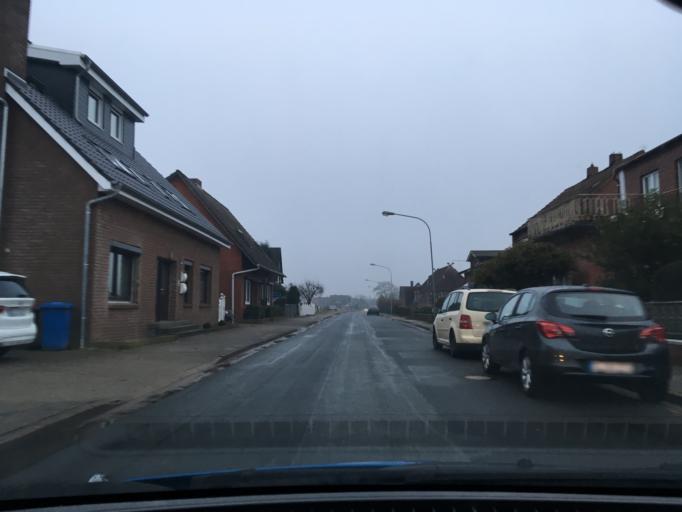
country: DE
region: Lower Saxony
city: Stelle
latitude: 53.4538
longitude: 10.0672
